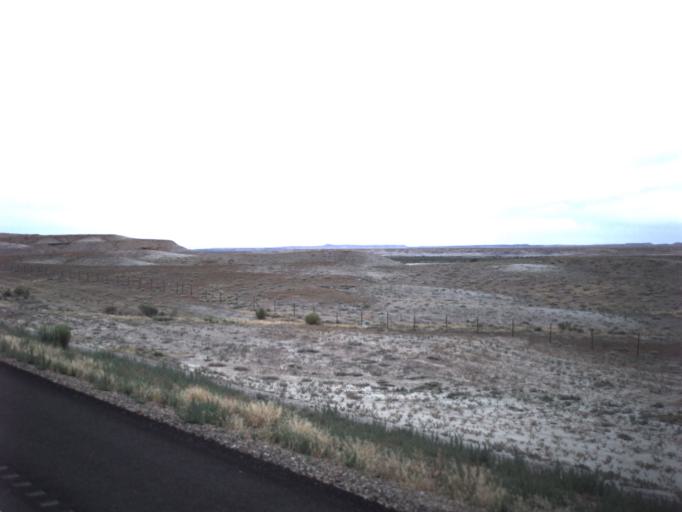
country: US
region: Utah
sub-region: Carbon County
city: East Carbon City
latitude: 38.9922
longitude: -110.2518
